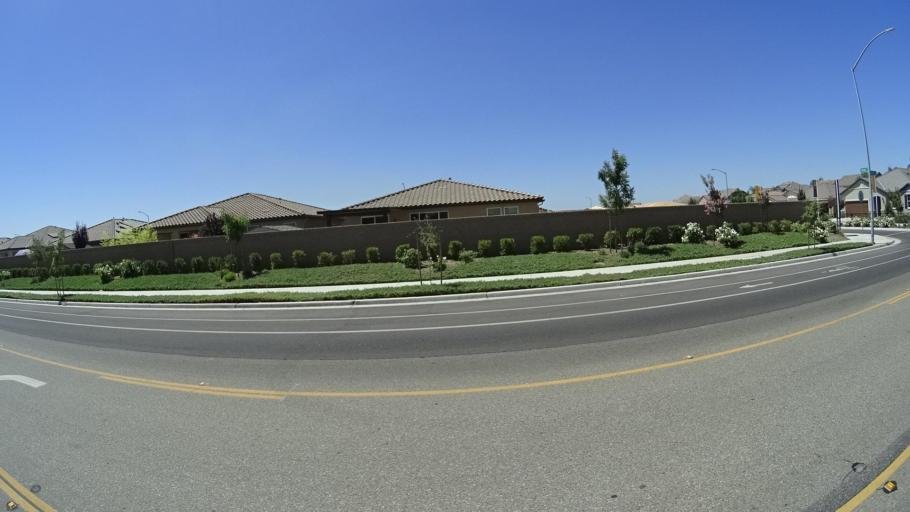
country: US
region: California
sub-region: Fresno County
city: Sunnyside
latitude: 36.7259
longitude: -119.6676
